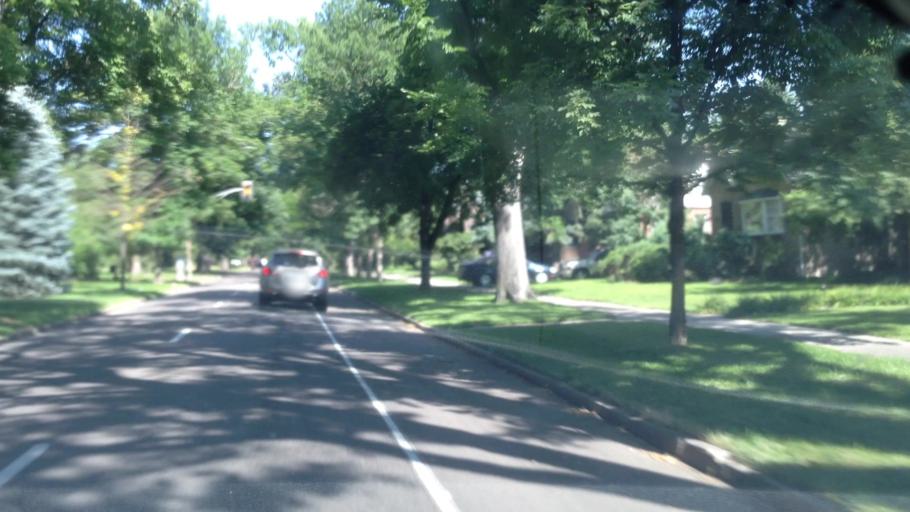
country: US
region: Colorado
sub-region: Arapahoe County
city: Glendale
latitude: 39.7434
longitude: -104.9370
